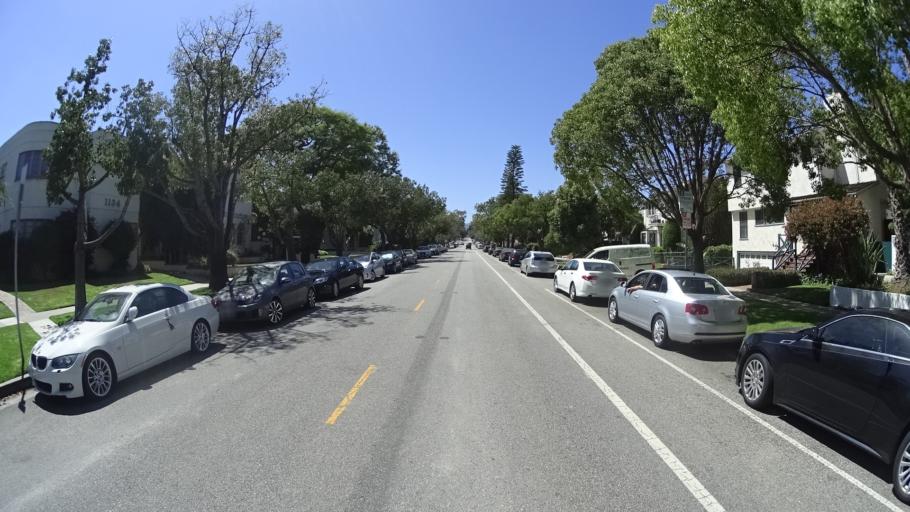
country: US
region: California
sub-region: Los Angeles County
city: Santa Monica
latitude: 34.0296
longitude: -118.4866
